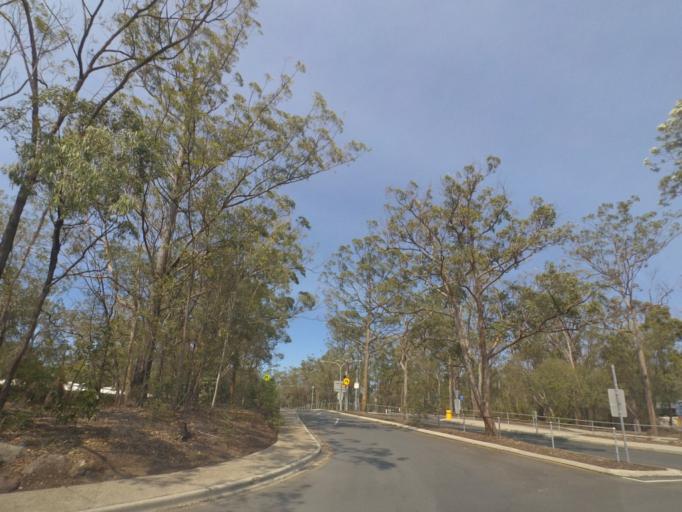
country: AU
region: Queensland
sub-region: Brisbane
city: Nathan
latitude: -27.5540
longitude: 153.0555
